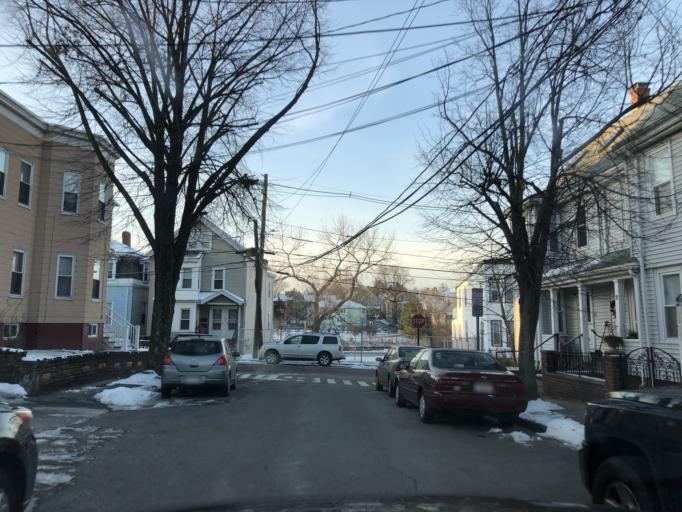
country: US
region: Massachusetts
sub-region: Middlesex County
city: Somerville
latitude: 42.3926
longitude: -71.1029
